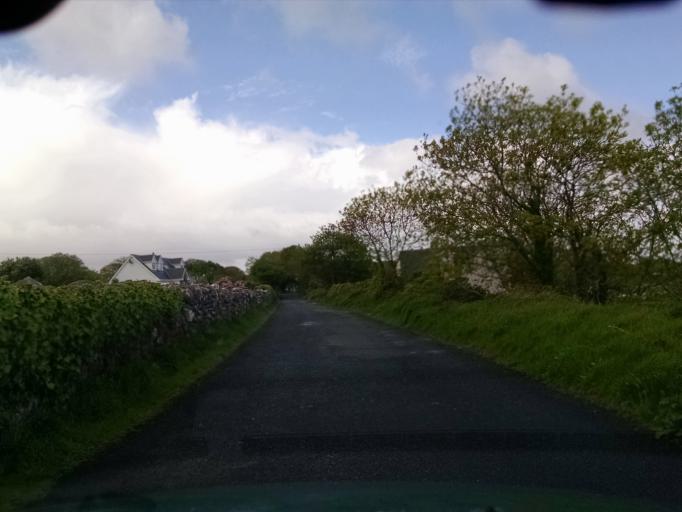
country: IE
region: Connaught
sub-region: County Galway
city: Bearna
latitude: 53.1559
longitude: -9.0795
